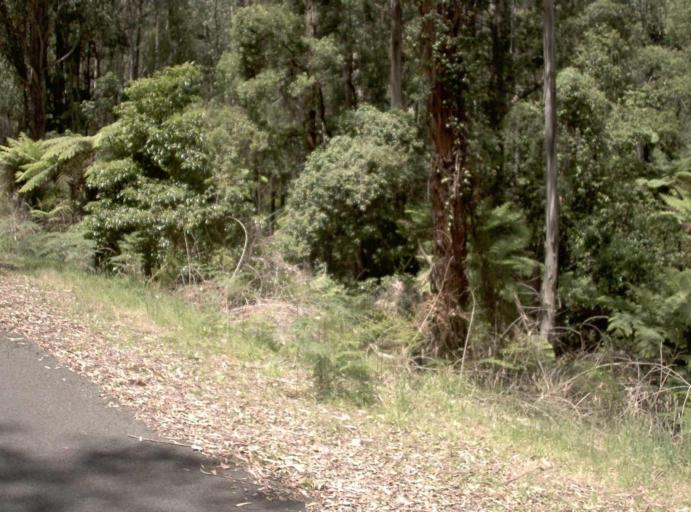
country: AU
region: New South Wales
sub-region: Bombala
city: Bombala
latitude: -37.4874
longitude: 148.9281
